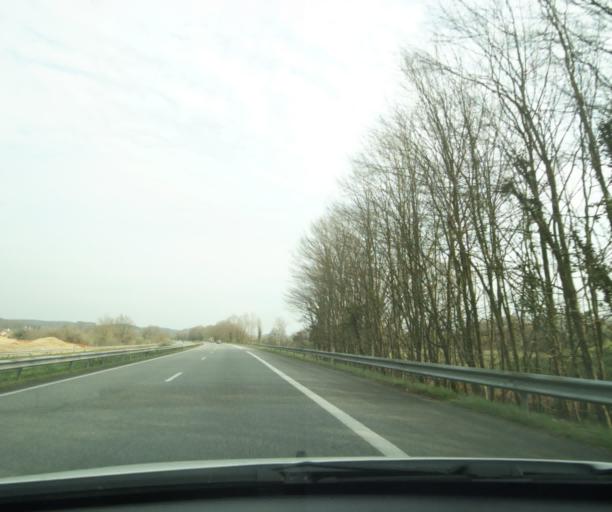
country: FR
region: Aquitaine
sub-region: Departement des Pyrenees-Atlantiques
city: Artix
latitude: 43.3860
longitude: -0.5299
